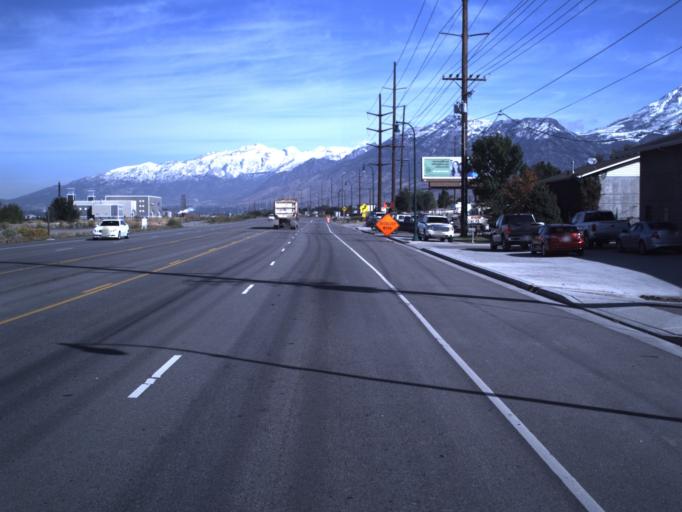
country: US
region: Utah
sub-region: Utah County
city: Orem
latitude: 40.3013
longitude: -111.7338
